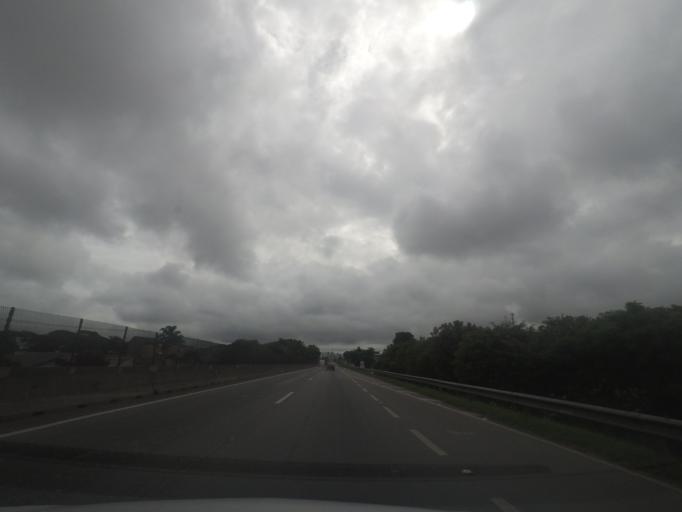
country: BR
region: Parana
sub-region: Pinhais
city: Pinhais
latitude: -25.4585
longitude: -49.2217
